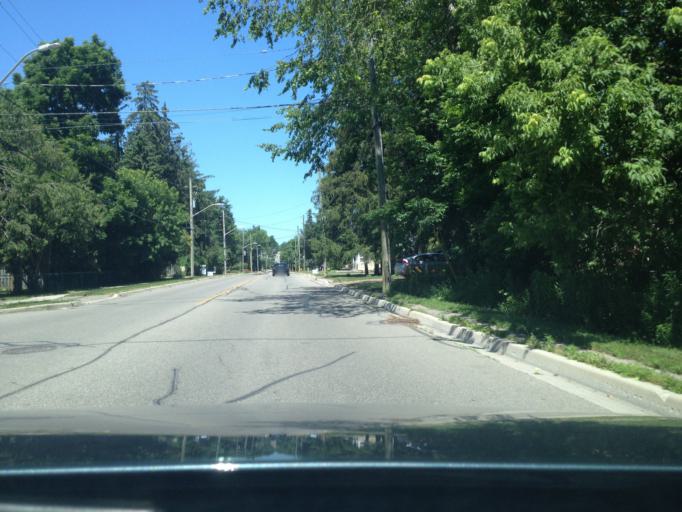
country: CA
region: Ontario
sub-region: Halton
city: Milton
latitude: 43.6648
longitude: -79.9228
